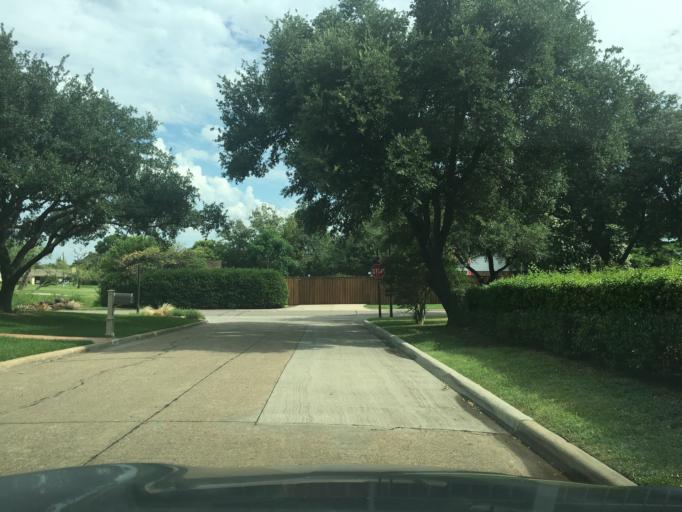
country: US
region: Texas
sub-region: Dallas County
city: Carrollton
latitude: 32.9411
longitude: -96.8621
